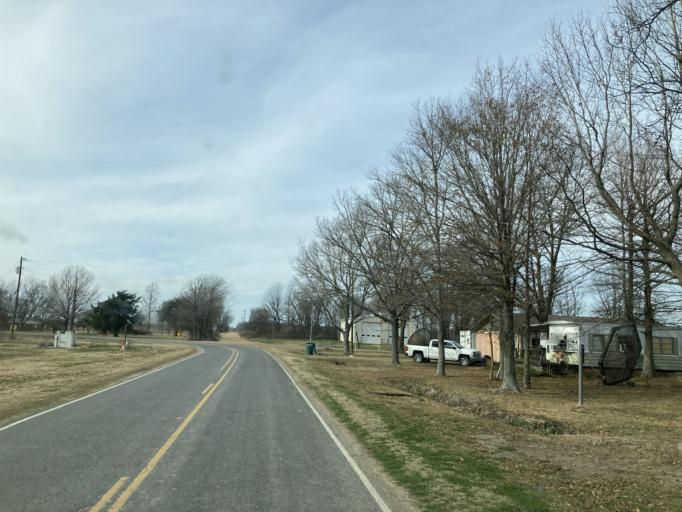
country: US
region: Mississippi
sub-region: Humphreys County
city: Belzoni
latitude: 33.1382
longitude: -90.6060
